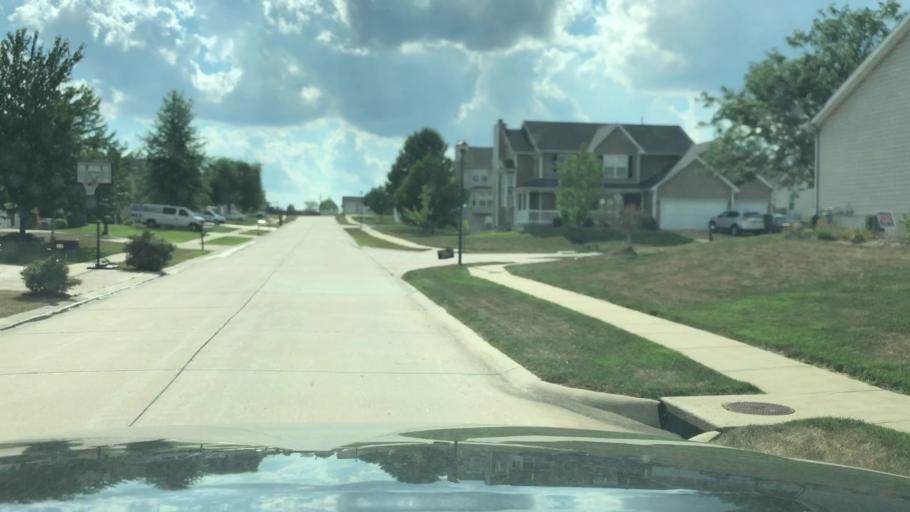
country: US
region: Missouri
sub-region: Saint Charles County
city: Wentzville
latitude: 38.8374
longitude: -90.8887
